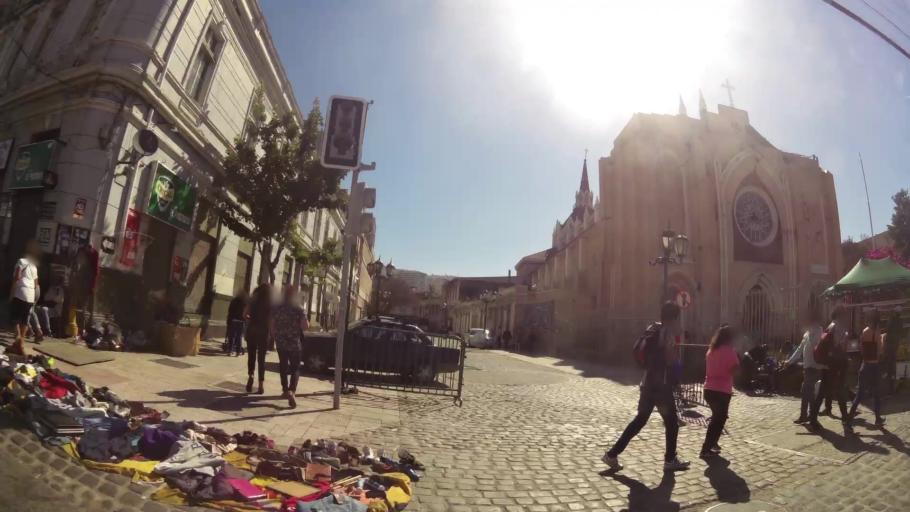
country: CL
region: Valparaiso
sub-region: Provincia de Valparaiso
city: Valparaiso
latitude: -33.0483
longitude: -71.6039
